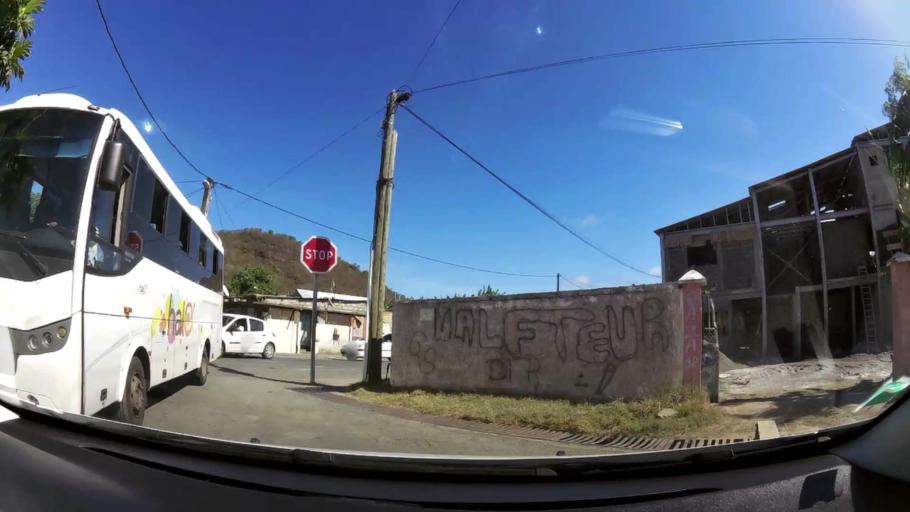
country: YT
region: Pamandzi
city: Pamandzi
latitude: -12.7857
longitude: 45.2760
